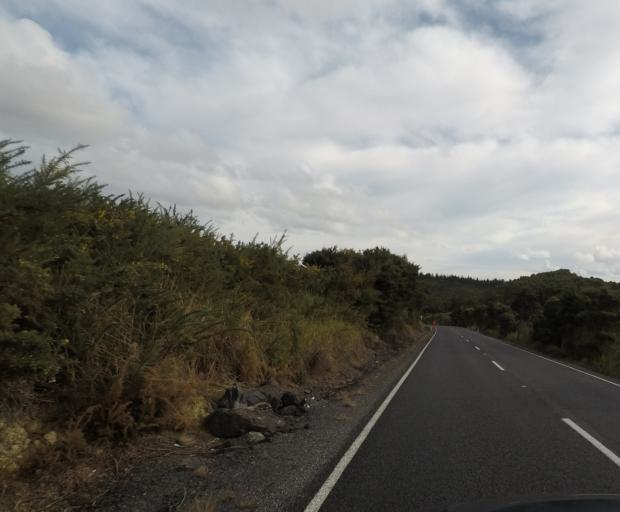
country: NZ
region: Northland
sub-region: Whangarei
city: Ruakaka
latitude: -36.0575
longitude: 174.5589
